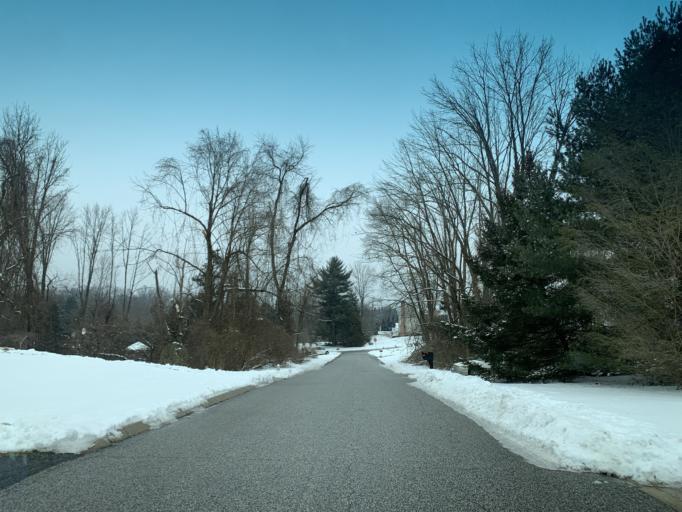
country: US
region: Maryland
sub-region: Harford County
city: Pleasant Hills
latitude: 39.5077
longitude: -76.3762
